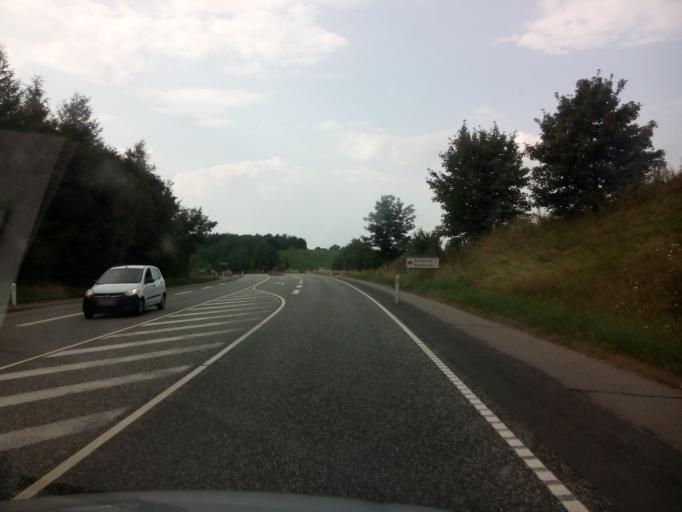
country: DK
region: Central Jutland
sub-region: Skanderborg Kommune
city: Skanderborg
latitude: 56.0647
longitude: 9.8570
